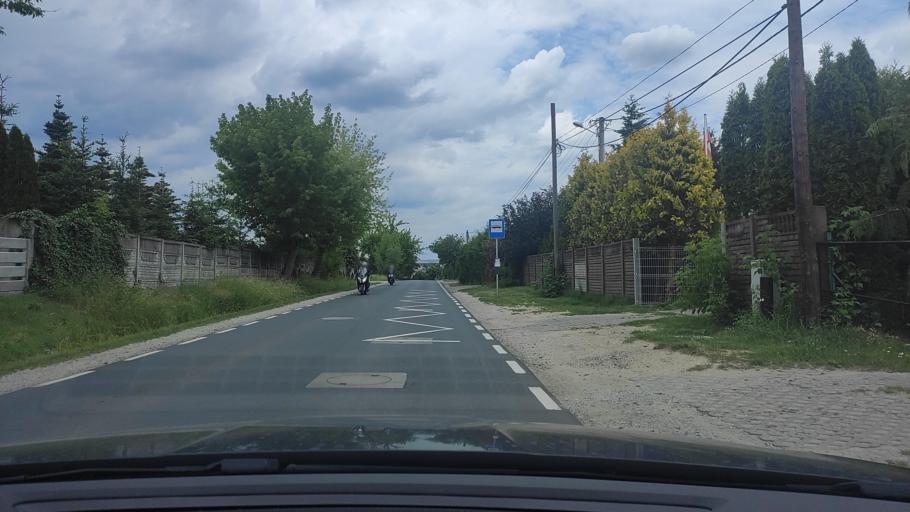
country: PL
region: Greater Poland Voivodeship
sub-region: Powiat poznanski
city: Kostrzyn
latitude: 52.4588
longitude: 17.1671
